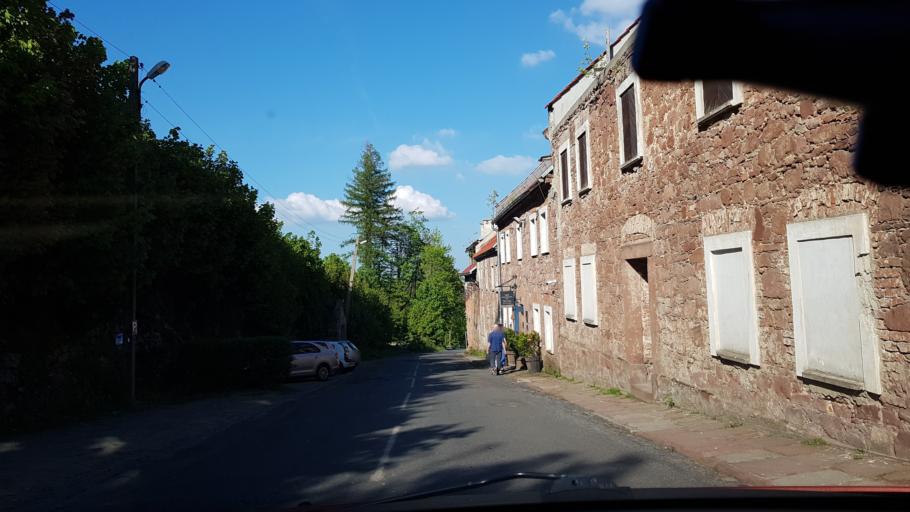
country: PL
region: Lower Silesian Voivodeship
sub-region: Powiat zabkowicki
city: Budzow
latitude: 50.5741
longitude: 16.6494
